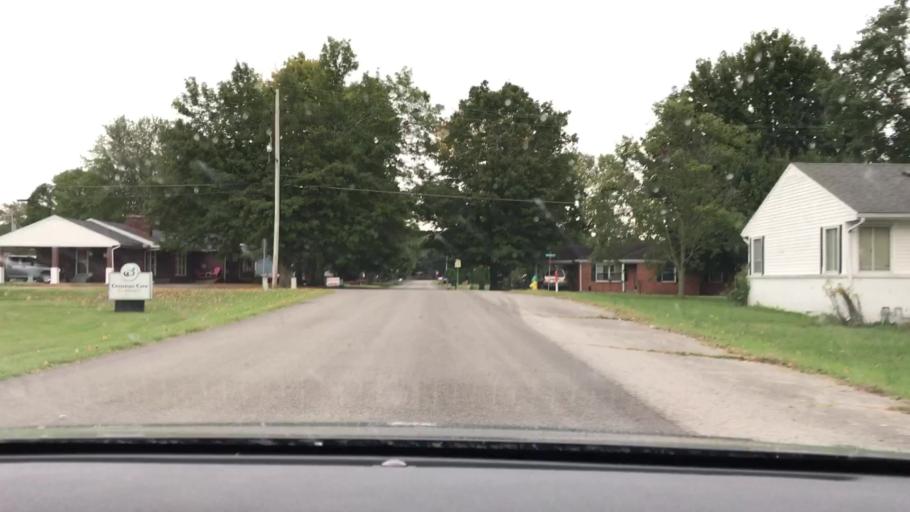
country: US
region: Kentucky
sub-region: Christian County
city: Hopkinsville
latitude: 36.8564
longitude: -87.5037
